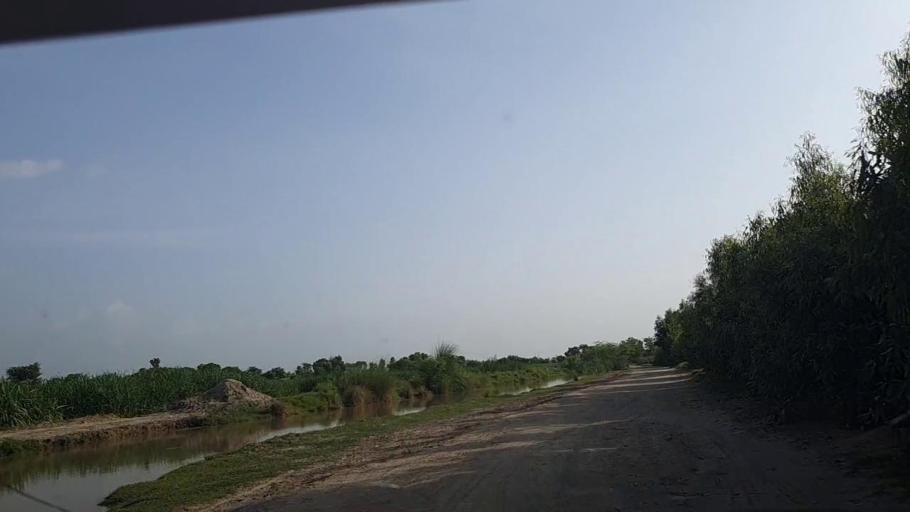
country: PK
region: Sindh
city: Ghotki
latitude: 27.9968
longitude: 69.2615
